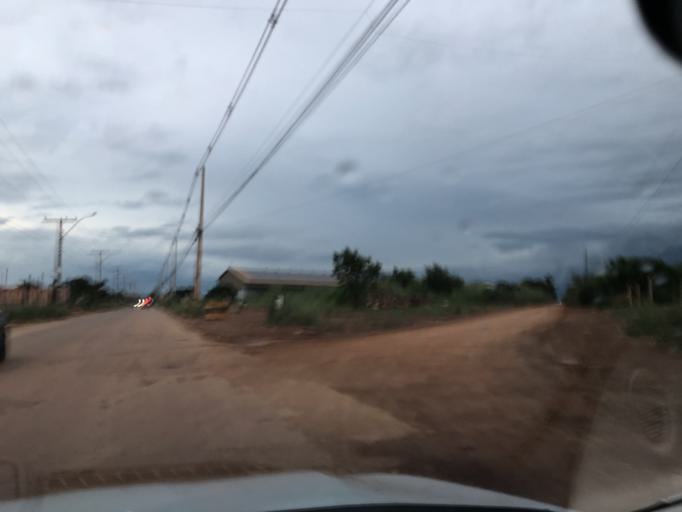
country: BR
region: Goias
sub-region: Luziania
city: Luziania
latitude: -16.1083
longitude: -47.9798
